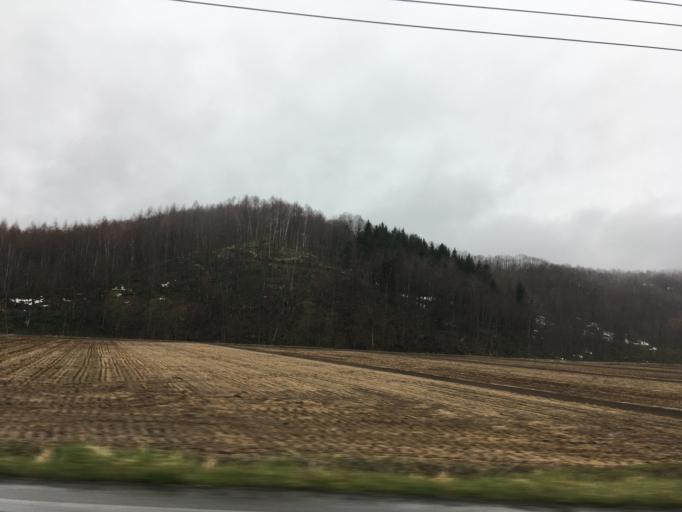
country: JP
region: Hokkaido
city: Nayoro
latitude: 44.0899
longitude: 142.4463
